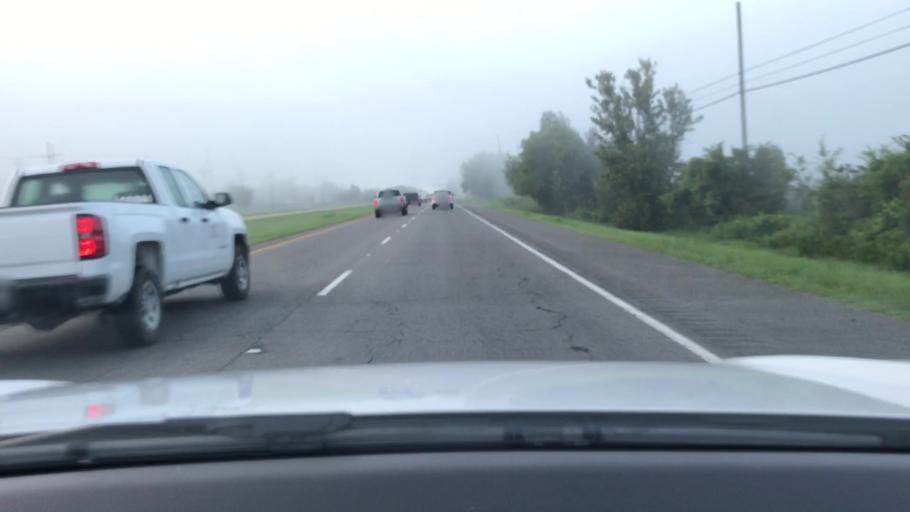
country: US
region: Louisiana
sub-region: West Baton Rouge Parish
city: Addis
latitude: 30.3366
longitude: -91.2590
